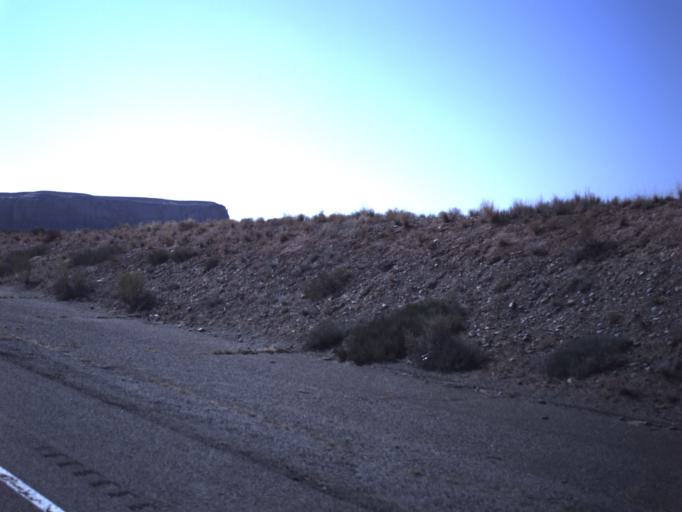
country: US
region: Utah
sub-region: San Juan County
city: Blanding
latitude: 37.2544
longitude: -109.6152
